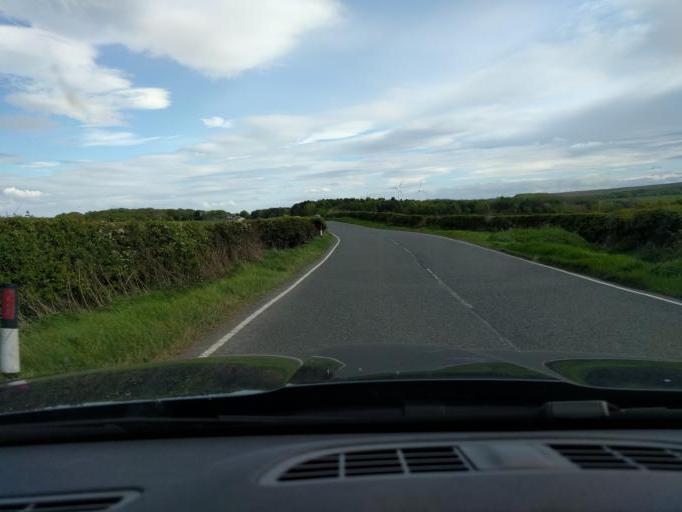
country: GB
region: England
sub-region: Northumberland
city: Bedlington
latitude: 55.1222
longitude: -1.6301
